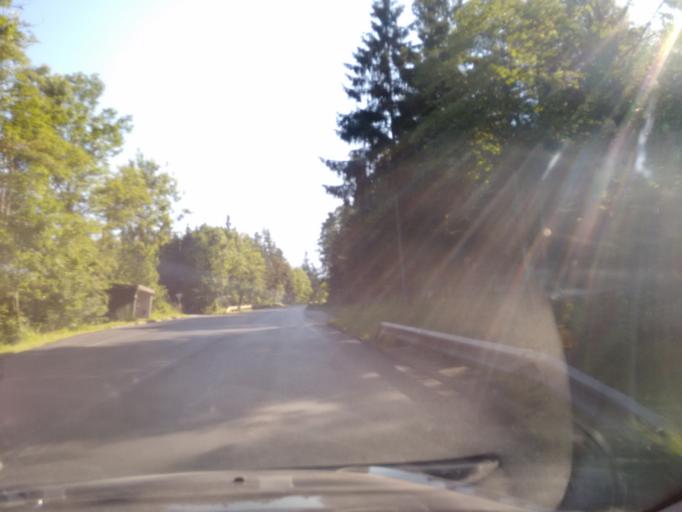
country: AT
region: Upper Austria
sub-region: Politischer Bezirk Gmunden
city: Bad Goisern
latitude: 47.6193
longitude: 13.6705
